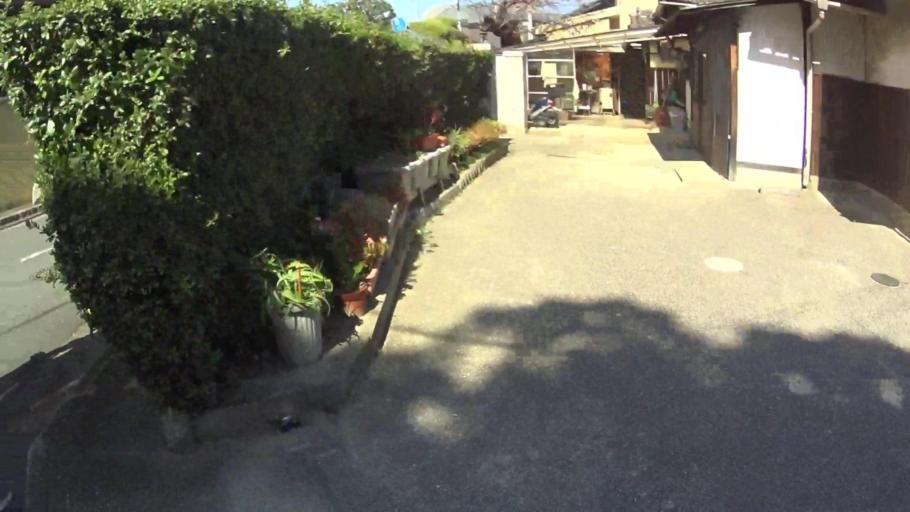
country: JP
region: Osaka
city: Izumiotsu
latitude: 34.4907
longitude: 135.4111
